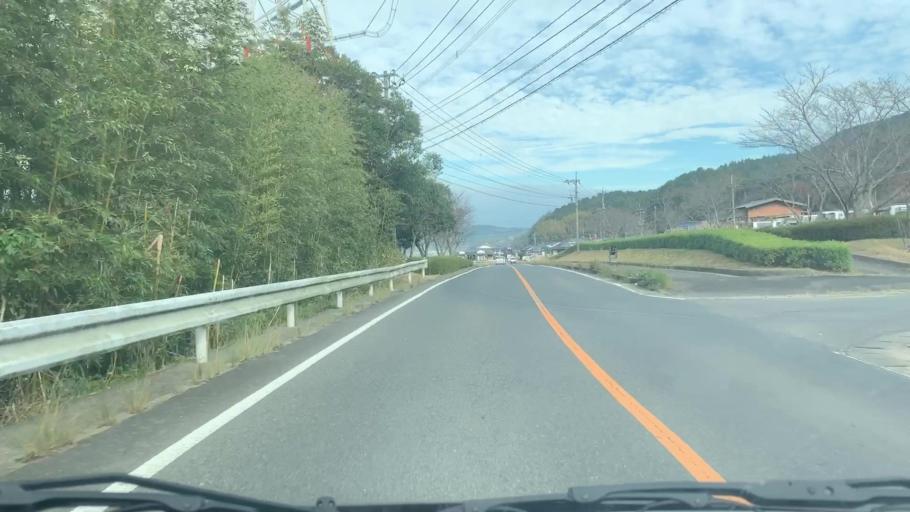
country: JP
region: Saga Prefecture
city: Karatsu
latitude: 33.3845
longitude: 129.9885
